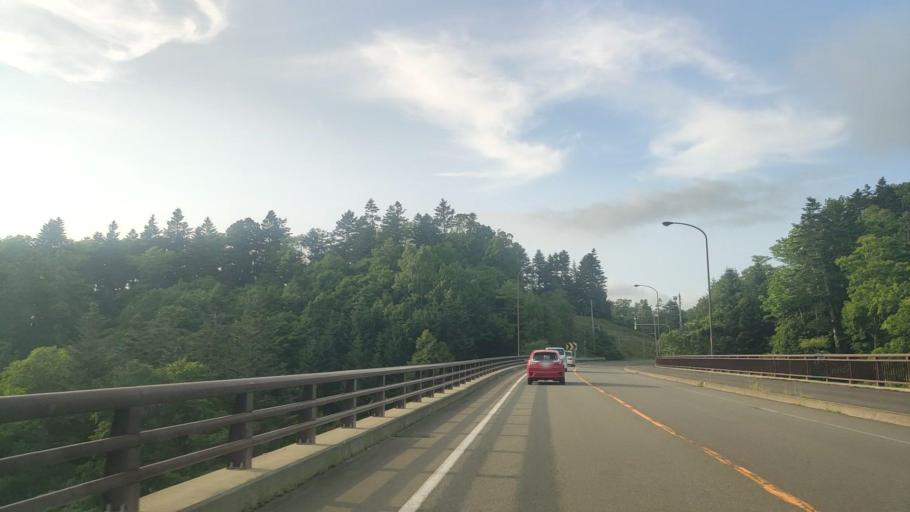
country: JP
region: Hokkaido
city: Iwamizawa
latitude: 43.0253
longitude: 141.9540
